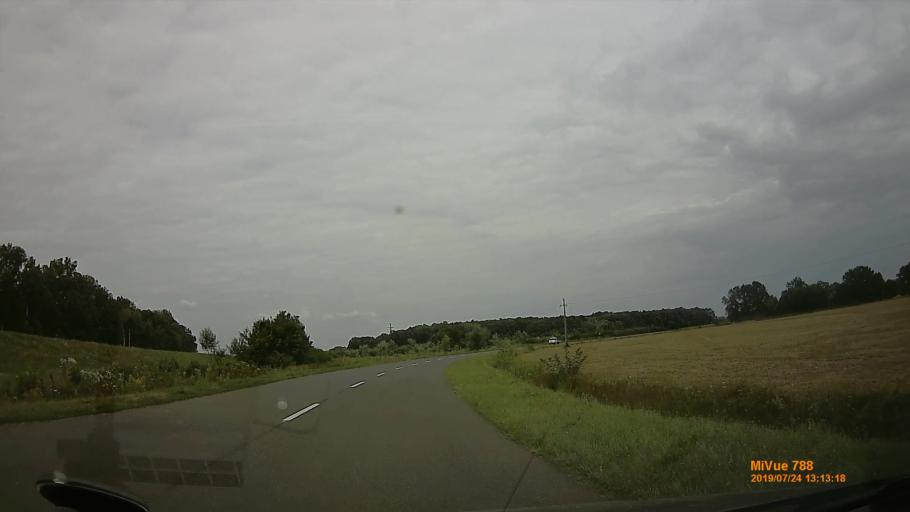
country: HU
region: Szabolcs-Szatmar-Bereg
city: Vasarosnameny
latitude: 48.1694
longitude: 22.3379
